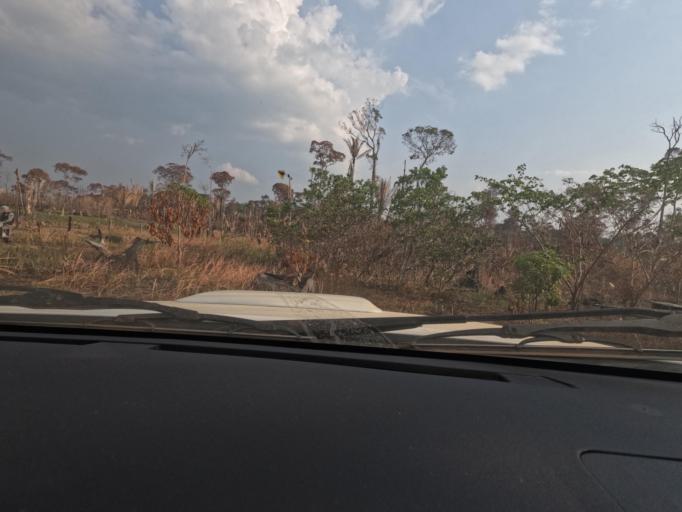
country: BR
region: Rondonia
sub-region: Porto Velho
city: Porto Velho
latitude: -8.5616
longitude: -64.0513
